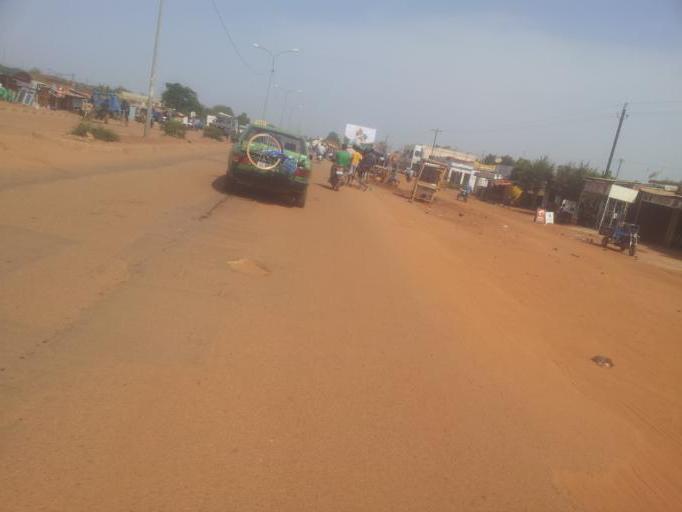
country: BF
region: Centre
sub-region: Kadiogo Province
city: Ouagadougou
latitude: 12.3894
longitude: -1.5750
